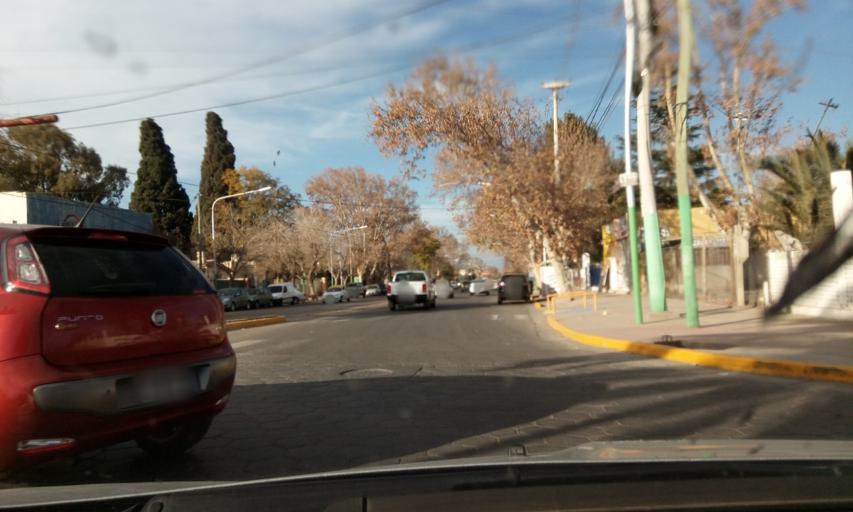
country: AR
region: San Juan
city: San Juan
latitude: -31.5305
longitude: -68.5944
